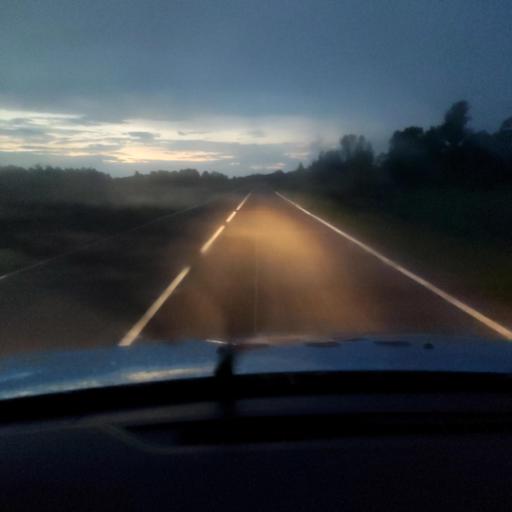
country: RU
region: Bashkortostan
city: Ulukulevo
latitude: 54.5220
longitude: 56.4103
